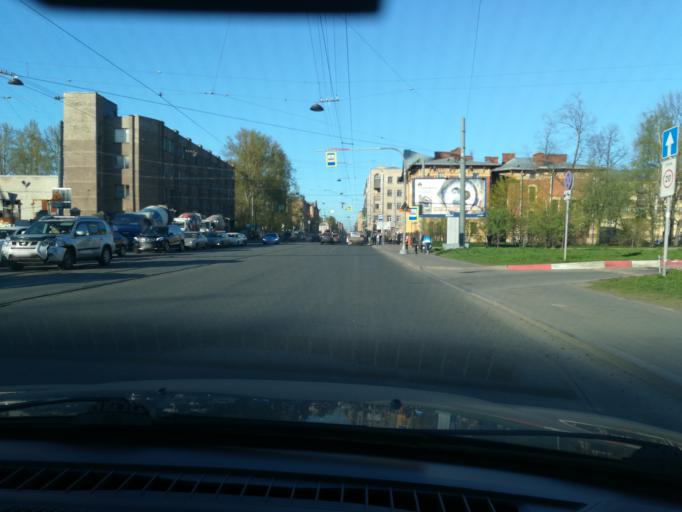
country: RU
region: St.-Petersburg
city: Vasyl'evsky Ostrov
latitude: 59.9365
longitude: 30.2563
